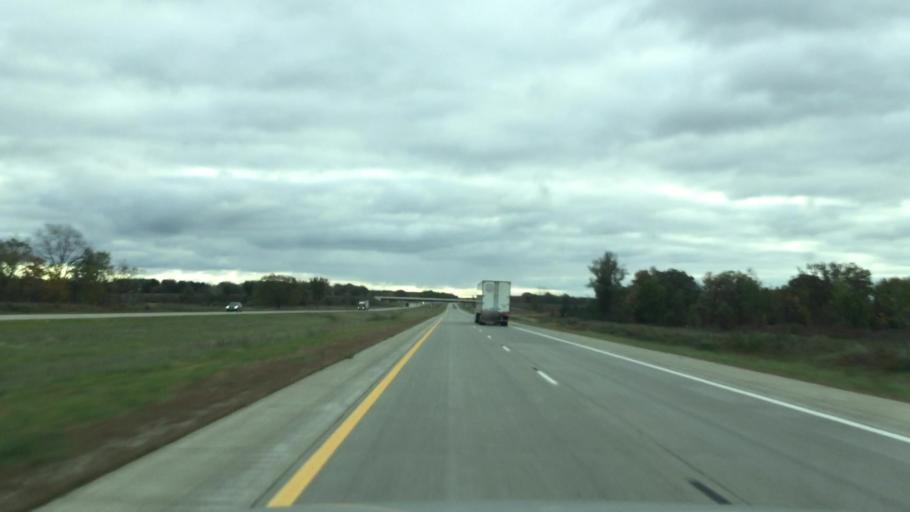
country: US
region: Michigan
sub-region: Saint Clair County
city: Capac
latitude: 42.9948
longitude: -82.9772
